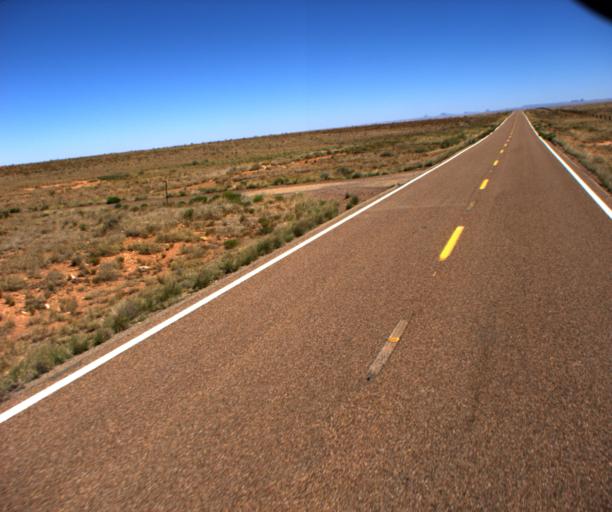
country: US
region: Arizona
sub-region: Navajo County
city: Winslow
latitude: 34.8757
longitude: -110.6544
